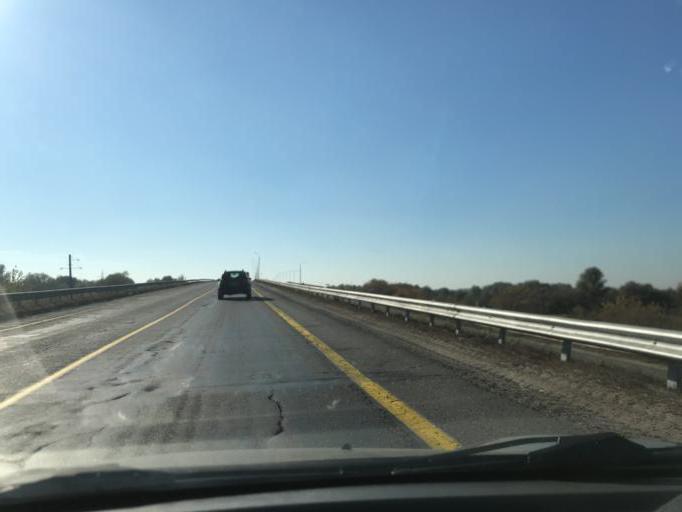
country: BY
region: Gomel
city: Horad Rechytsa
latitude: 52.3262
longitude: 30.5322
